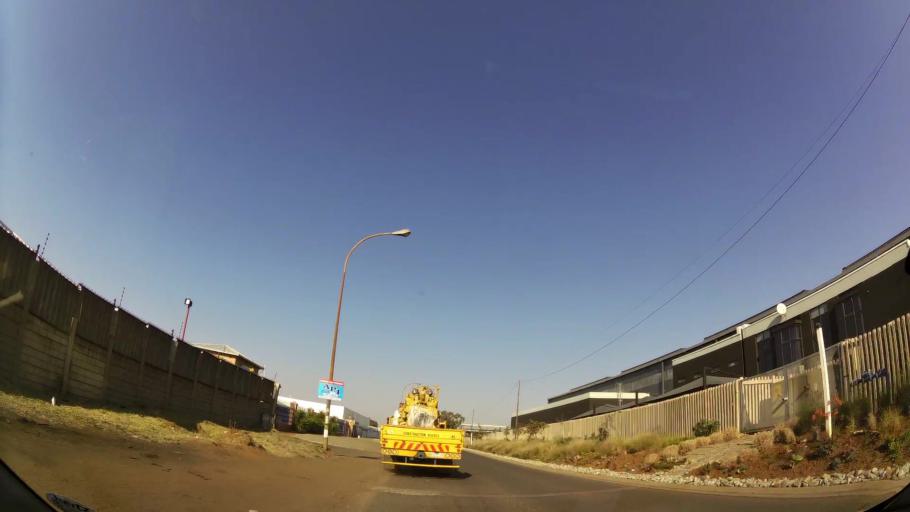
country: ZA
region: Gauteng
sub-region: Ekurhuleni Metropolitan Municipality
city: Germiston
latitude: -26.1702
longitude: 28.1968
